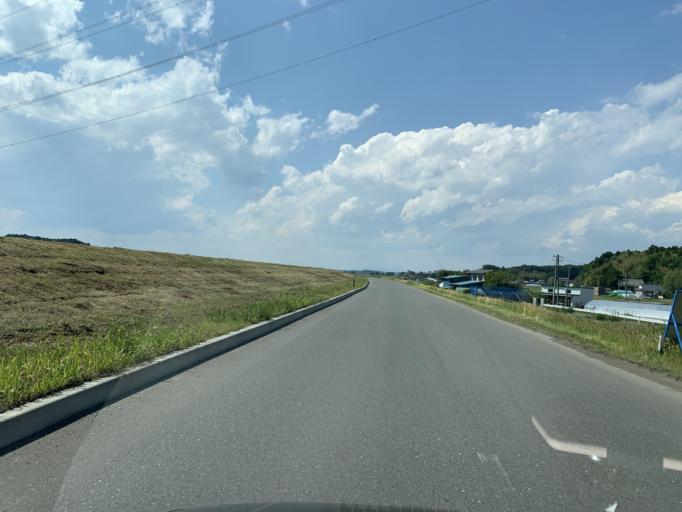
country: JP
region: Miyagi
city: Matsushima
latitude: 38.4302
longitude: 141.1241
